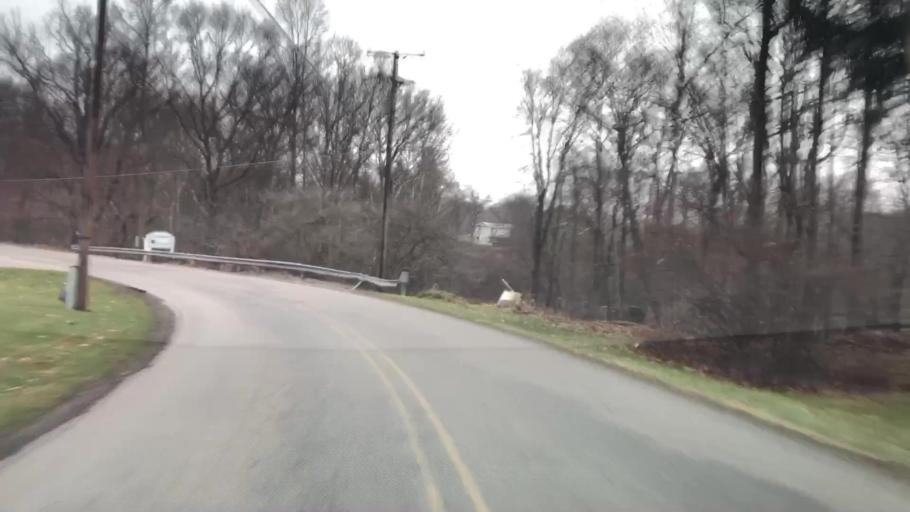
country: US
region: Pennsylvania
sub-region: Mercer County
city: Grove City
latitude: 41.1300
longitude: -80.0918
